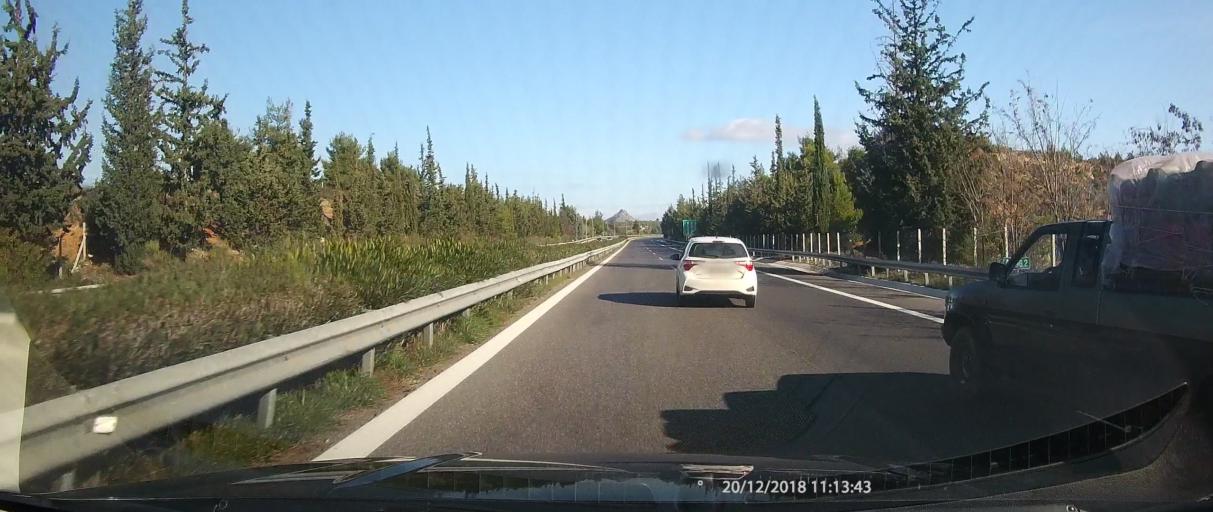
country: GR
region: Peloponnese
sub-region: Nomos Korinthias
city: Khiliomodhi
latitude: 37.8575
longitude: 22.8346
